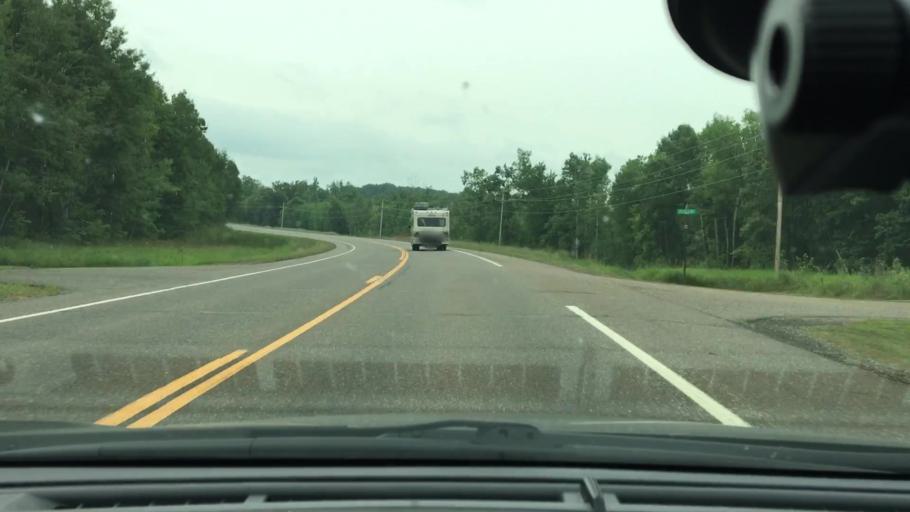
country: US
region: Minnesota
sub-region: Crow Wing County
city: Crosby
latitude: 46.5097
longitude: -93.9601
